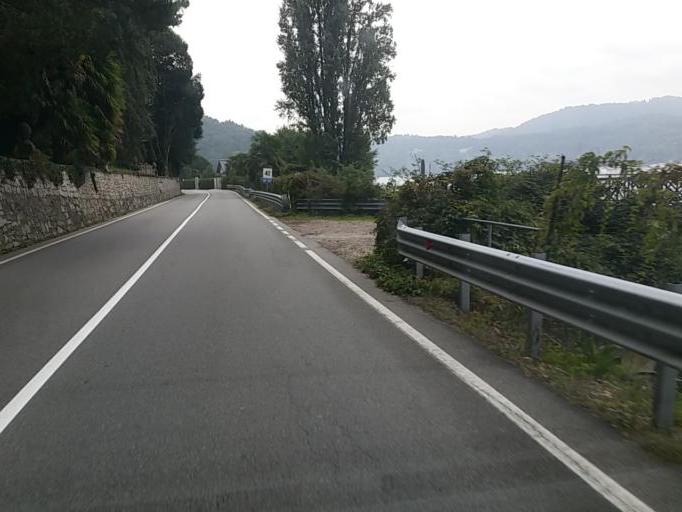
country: IT
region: Piedmont
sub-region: Provincia di Novara
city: Ameno
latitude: 45.7810
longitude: 8.4260
